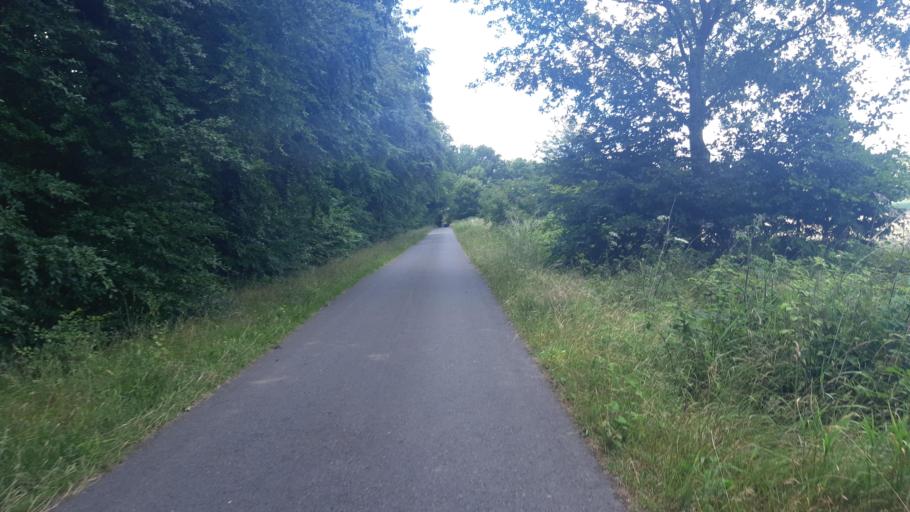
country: DE
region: Lower Saxony
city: Tosterglope
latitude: 53.2037
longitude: 10.8015
